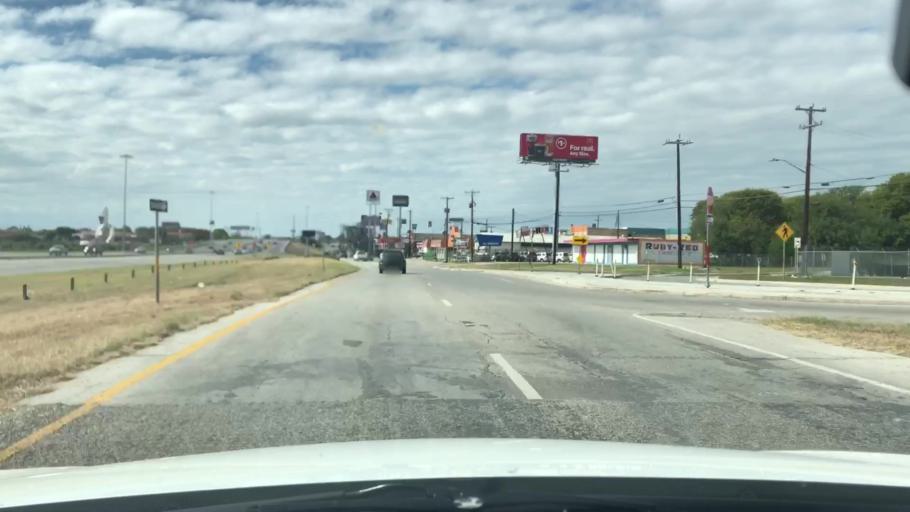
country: US
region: Texas
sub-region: Bexar County
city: Lackland Air Force Base
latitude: 29.4041
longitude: -98.6218
